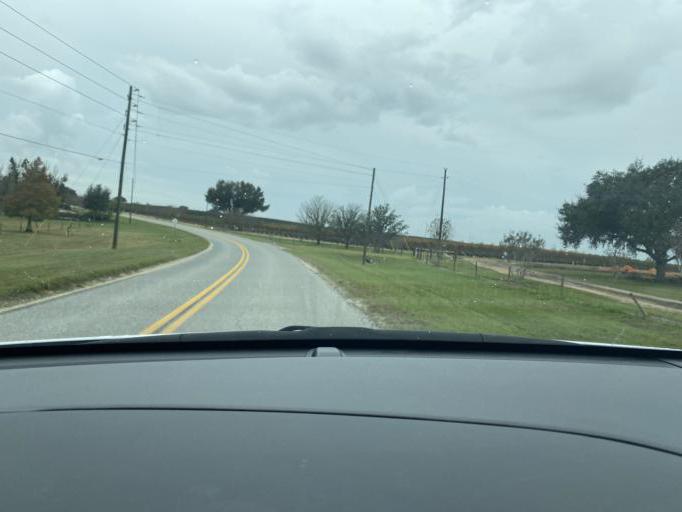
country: US
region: Florida
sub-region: Lake County
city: Groveland
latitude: 28.5998
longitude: -81.8261
